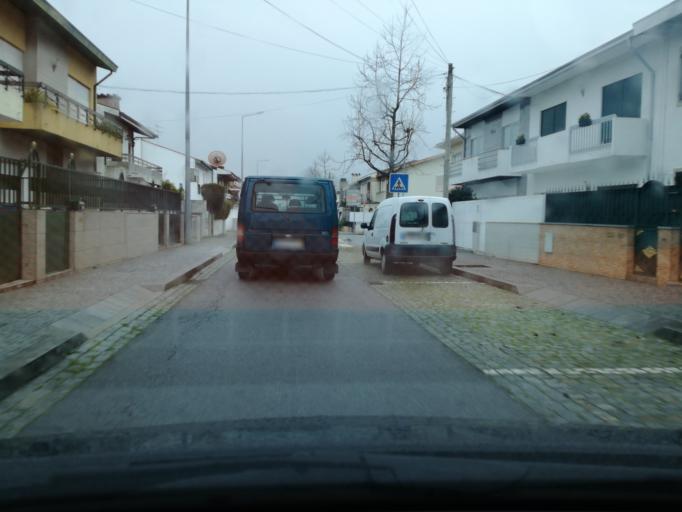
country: PT
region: Porto
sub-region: Maia
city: Gemunde
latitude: 41.2551
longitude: -8.6654
